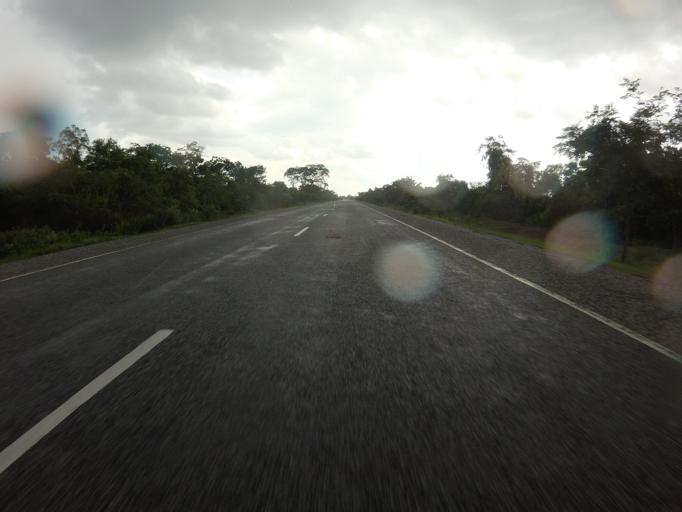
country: GH
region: Northern
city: Tamale
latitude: 9.1218
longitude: -1.6394
